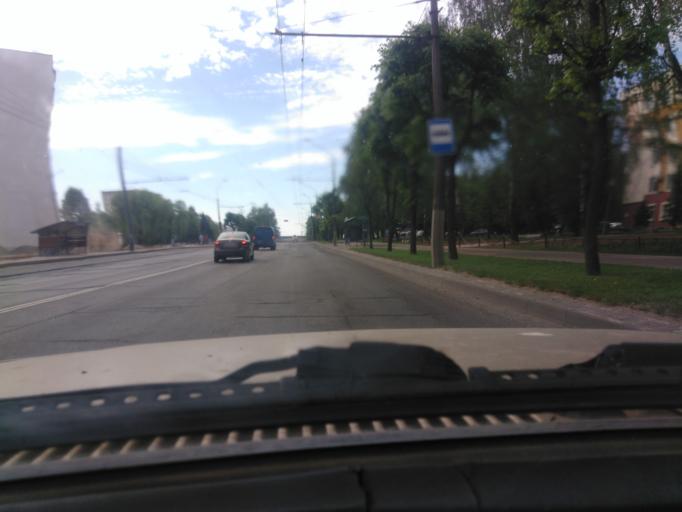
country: BY
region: Mogilev
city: Buynichy
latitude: 53.8956
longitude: 30.2965
